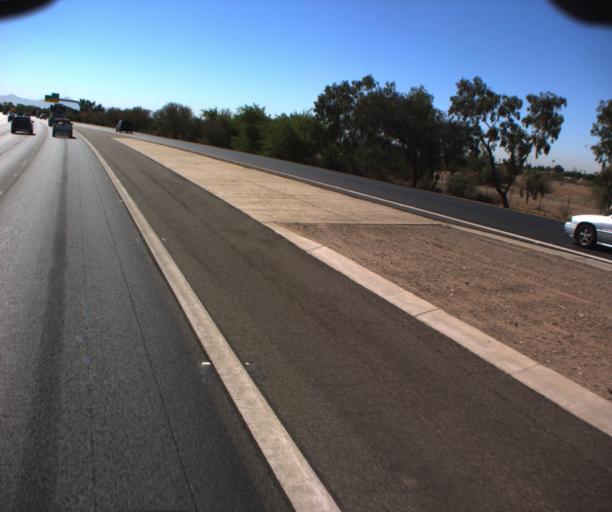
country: US
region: Arizona
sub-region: Maricopa County
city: Sun City
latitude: 33.5907
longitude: -112.2612
